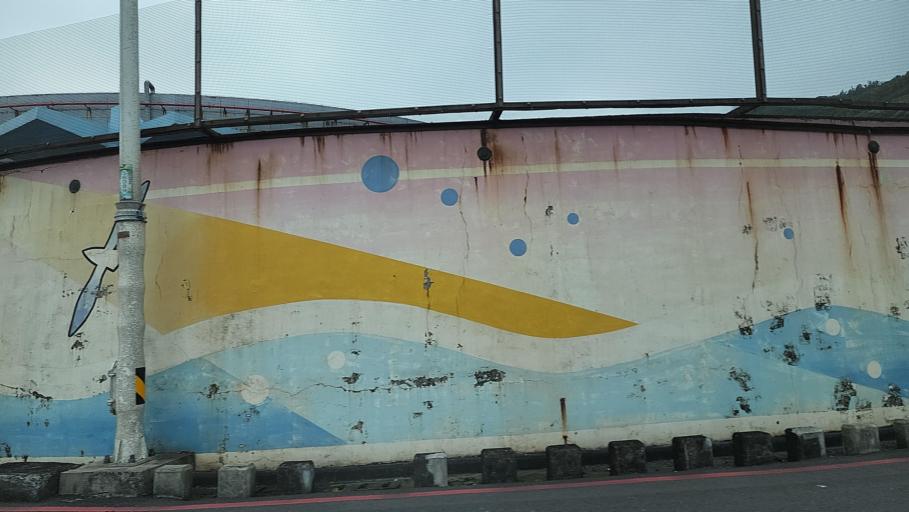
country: TW
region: Taiwan
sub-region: Keelung
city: Keelung
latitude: 25.1632
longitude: 121.7300
